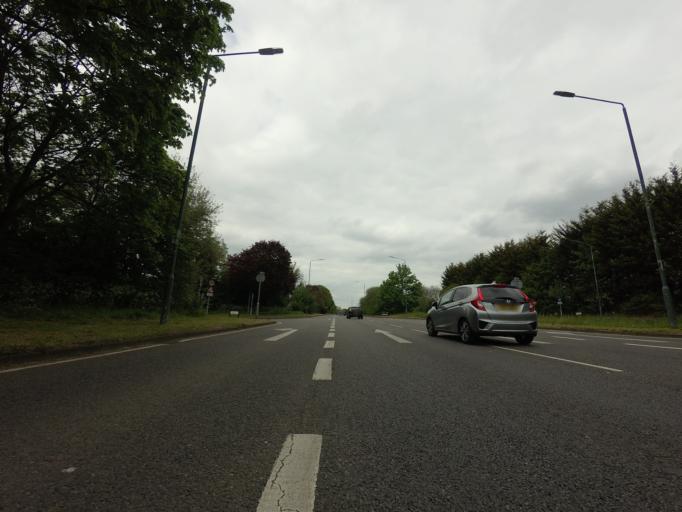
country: GB
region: England
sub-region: Greater London
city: Bexley
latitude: 51.4222
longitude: 0.1337
